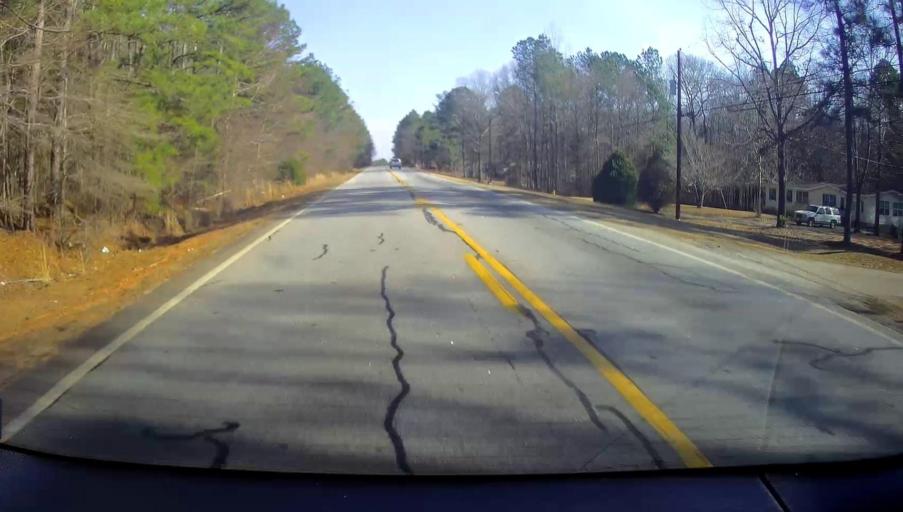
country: US
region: Georgia
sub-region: Butts County
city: Indian Springs
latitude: 33.2496
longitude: -83.8919
